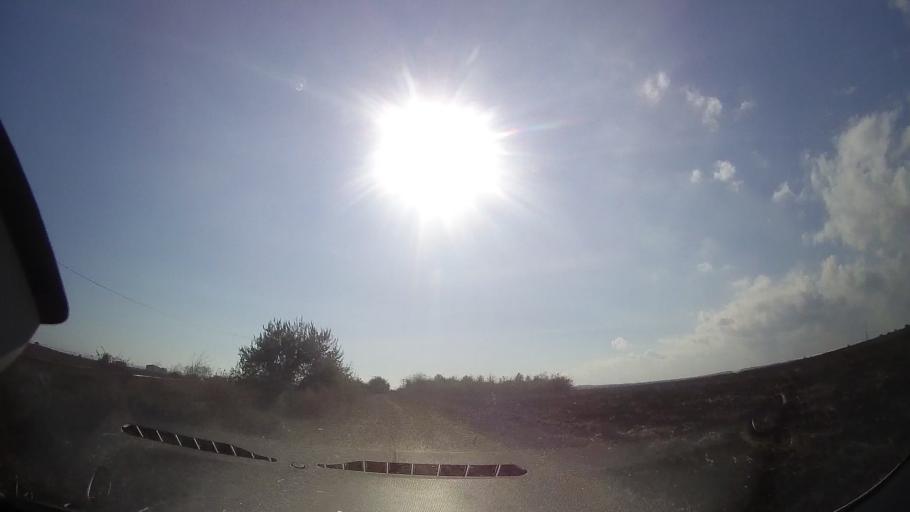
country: RO
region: Constanta
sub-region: Comuna Costinesti
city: Costinesti
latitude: 43.9748
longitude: 28.6440
